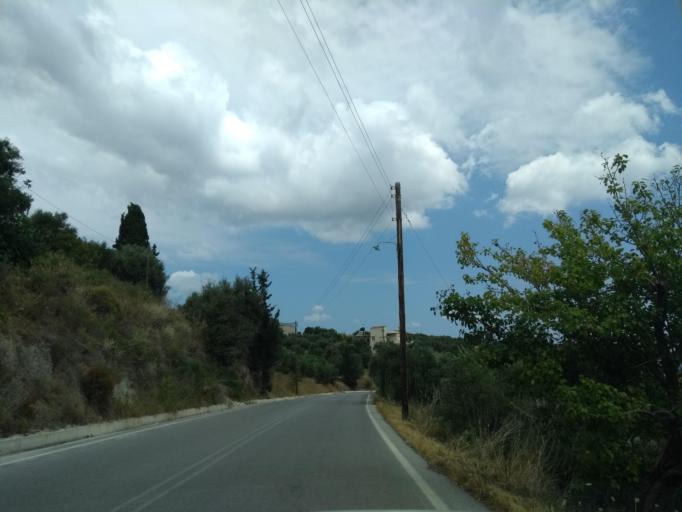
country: GR
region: Crete
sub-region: Nomos Chanias
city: Kalivai
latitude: 35.4351
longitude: 24.1762
